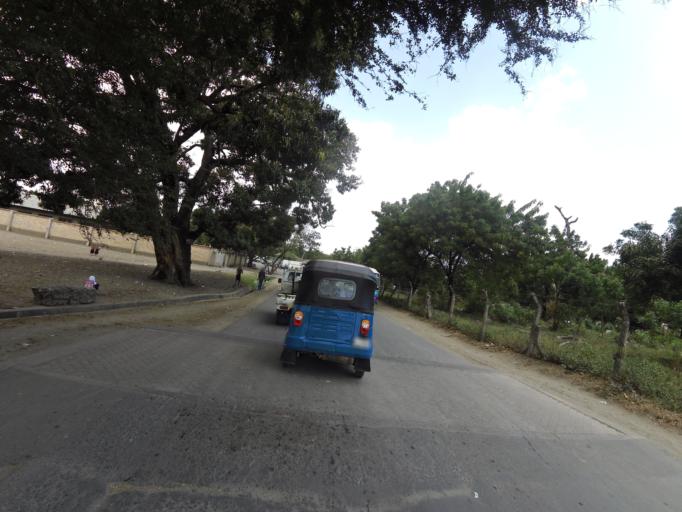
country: TZ
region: Dar es Salaam
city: Magomeni
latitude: -6.8013
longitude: 39.2558
